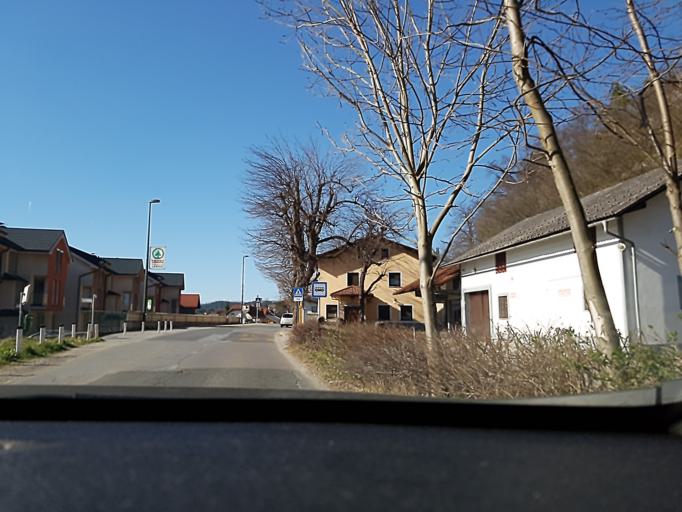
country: SI
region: Medvode
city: Zgornje Pirnice
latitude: 46.1283
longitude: 14.4448
